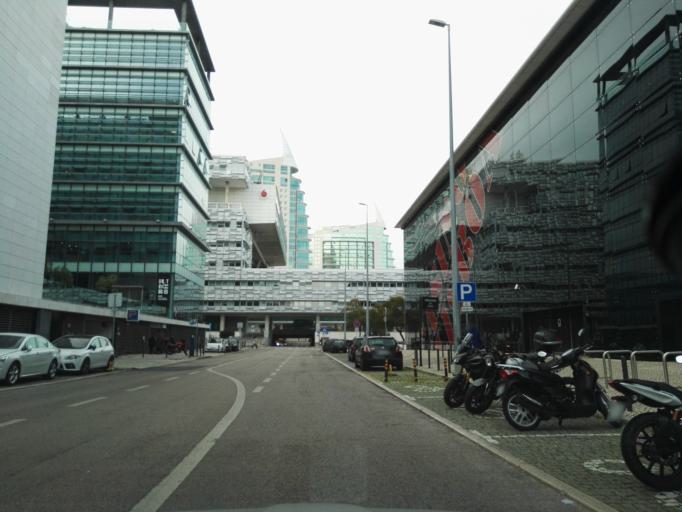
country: PT
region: Lisbon
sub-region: Loures
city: Moscavide
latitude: 38.7647
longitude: -9.0970
